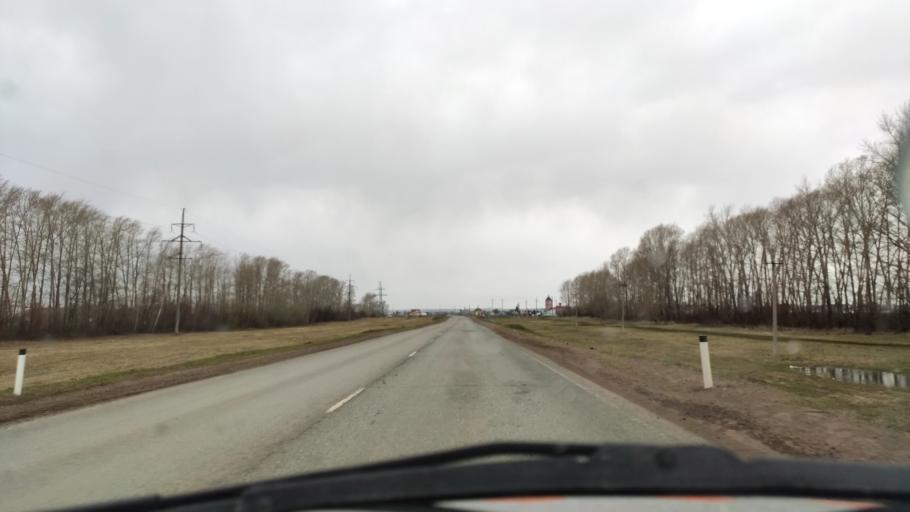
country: RU
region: Bashkortostan
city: Kushnarenkovo
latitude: 55.0759
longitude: 55.4025
